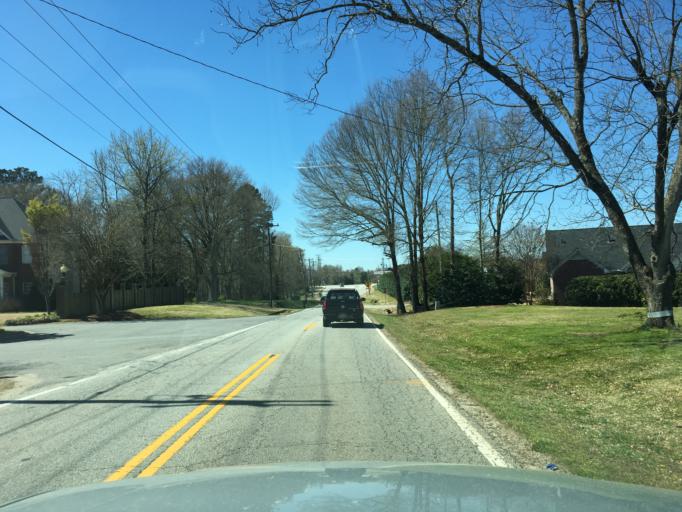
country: US
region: South Carolina
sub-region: Spartanburg County
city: Roebuck
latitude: 34.8911
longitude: -81.9693
